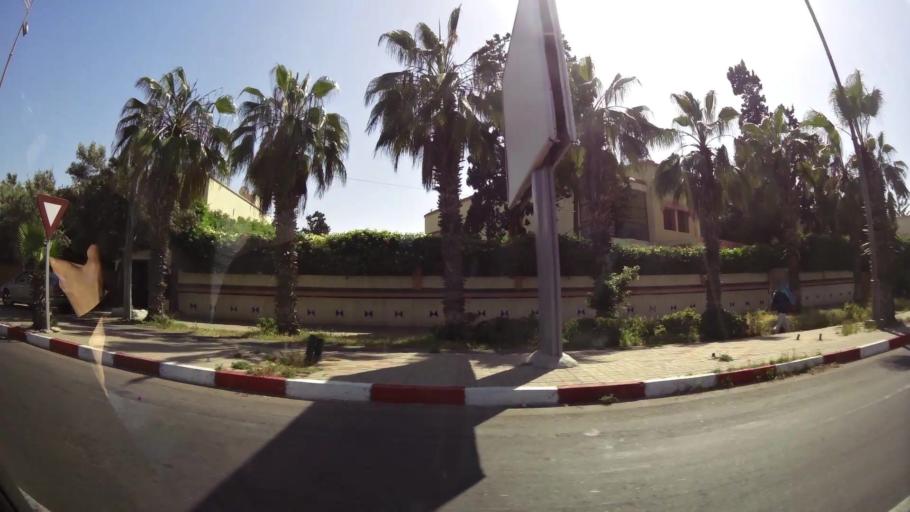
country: MA
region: Souss-Massa-Draa
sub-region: Inezgane-Ait Mellou
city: Inezgane
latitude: 30.3662
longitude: -9.5460
